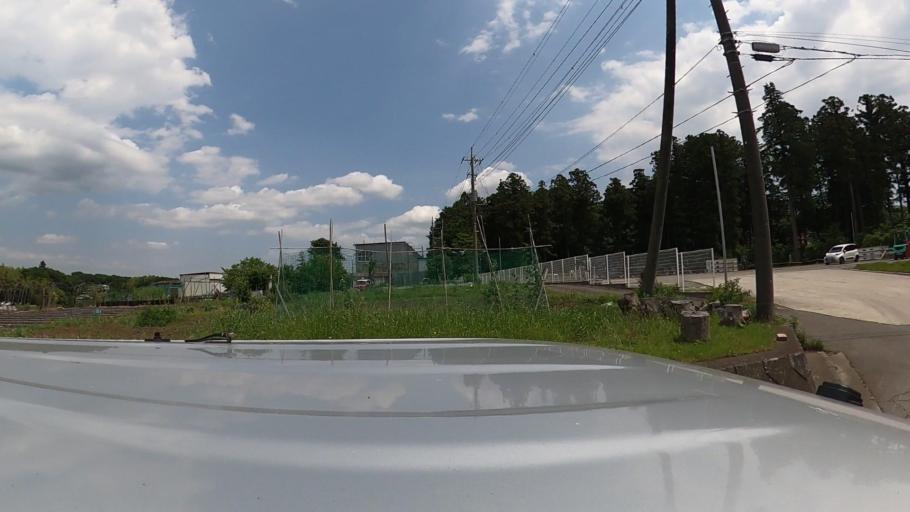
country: JP
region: Kanagawa
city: Chigasaki
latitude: 35.3929
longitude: 139.4209
